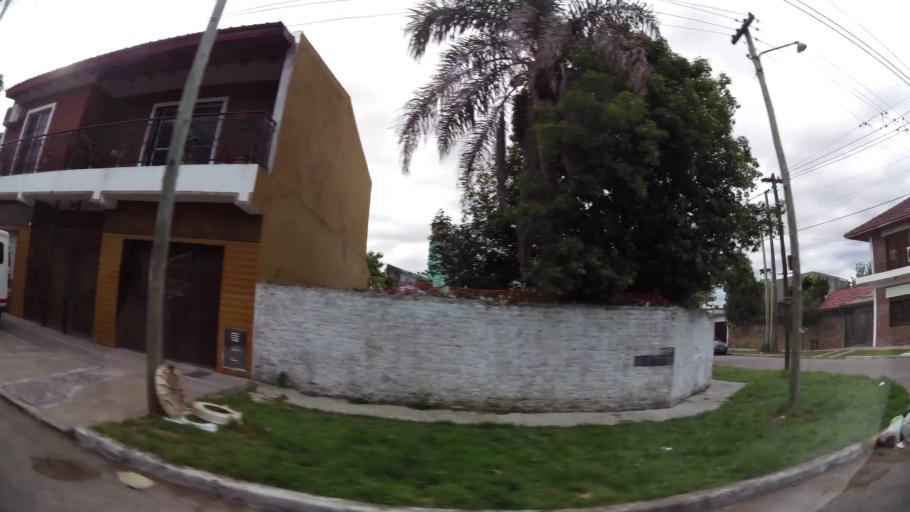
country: AR
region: Buenos Aires
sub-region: Partido de Quilmes
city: Quilmes
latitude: -34.7473
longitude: -58.2295
